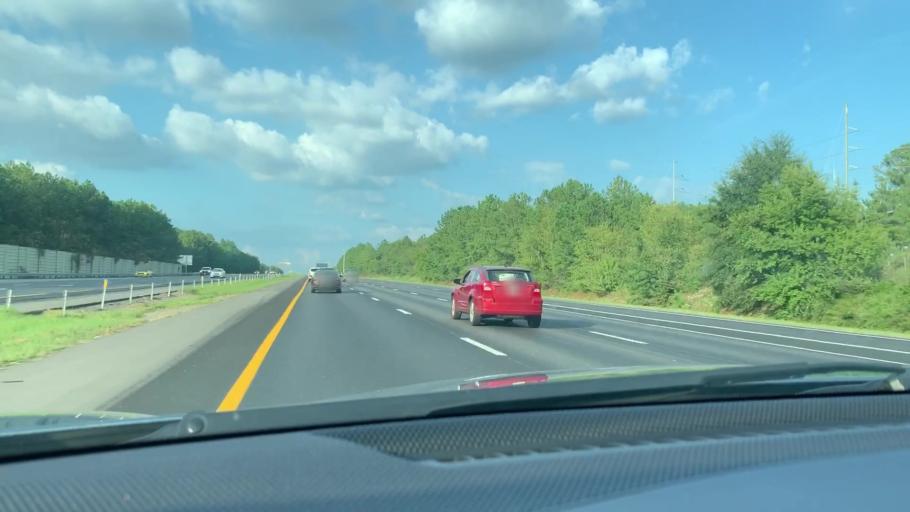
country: US
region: South Carolina
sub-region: Richland County
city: Woodfield
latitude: 34.0250
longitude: -80.9441
